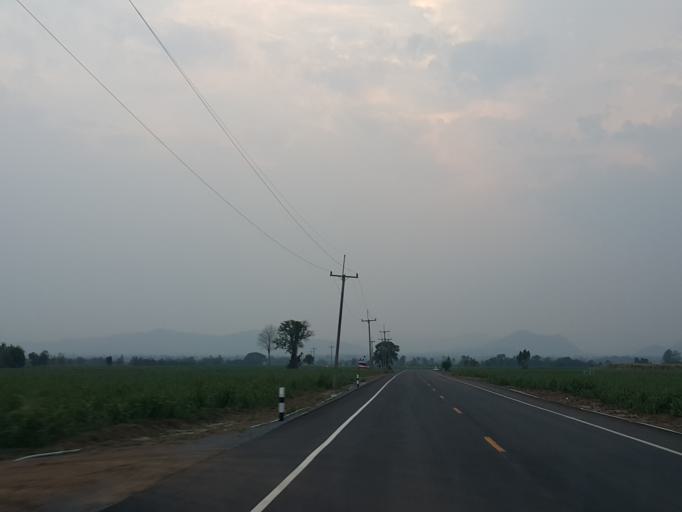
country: TH
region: Suphan Buri
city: Dan Chang
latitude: 14.9431
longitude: 99.6531
